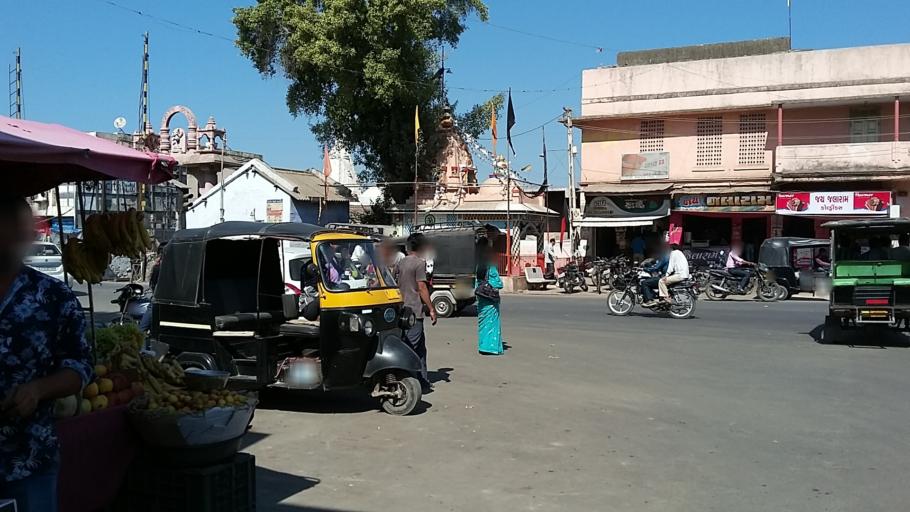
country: IN
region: Gujarat
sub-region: Junagadh
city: Junagadh
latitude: 21.5109
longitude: 70.4608
